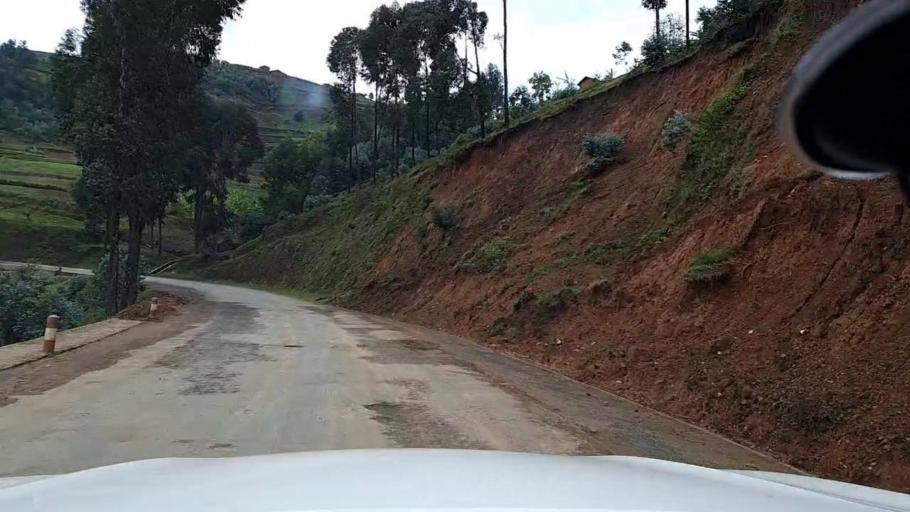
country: RW
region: Southern Province
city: Gitarama
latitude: -2.0663
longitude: 29.5530
